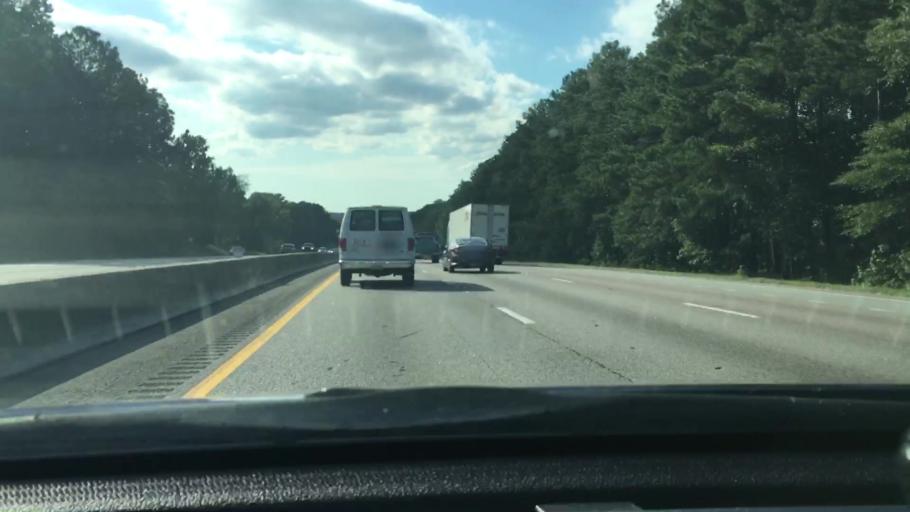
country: US
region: South Carolina
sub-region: Richland County
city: Forest Acres
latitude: 34.0662
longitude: -81.0283
